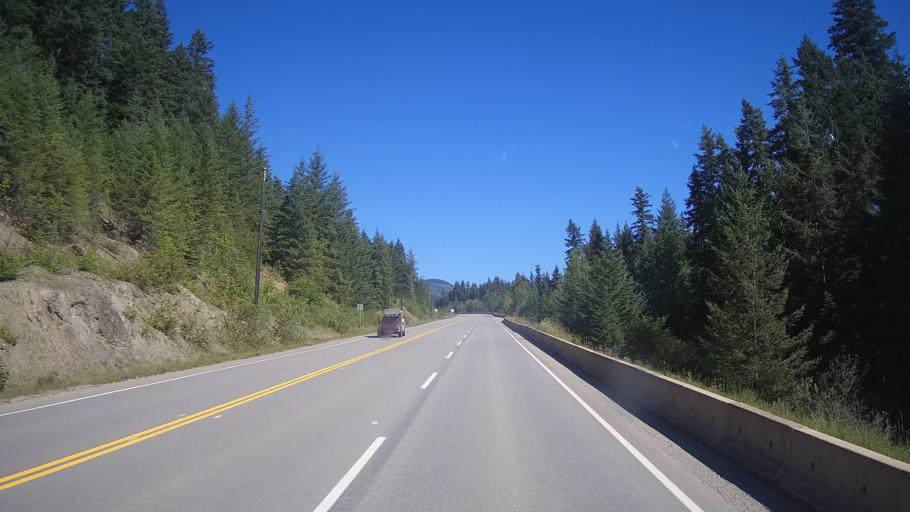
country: CA
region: British Columbia
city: Kamloops
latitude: 51.4590
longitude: -120.2292
